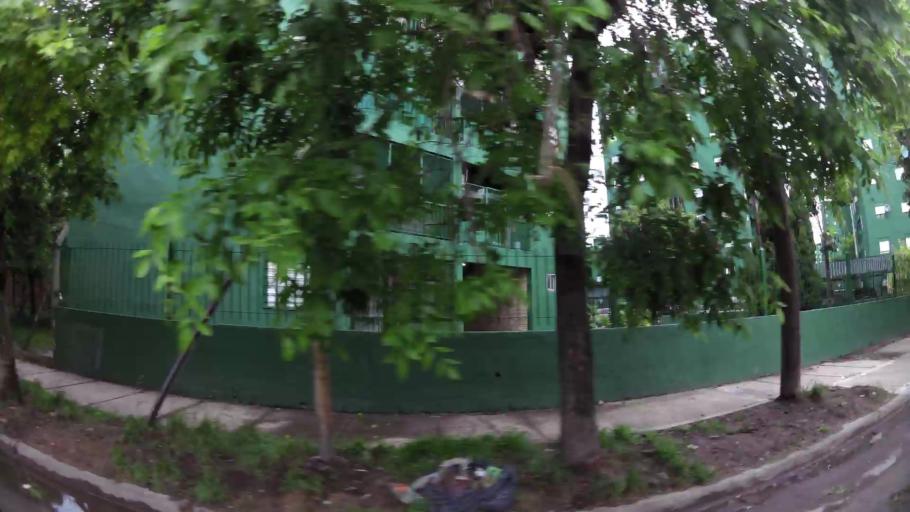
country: AR
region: Buenos Aires
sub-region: Partido de Lanus
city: Lanus
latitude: -34.7088
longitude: -58.3572
